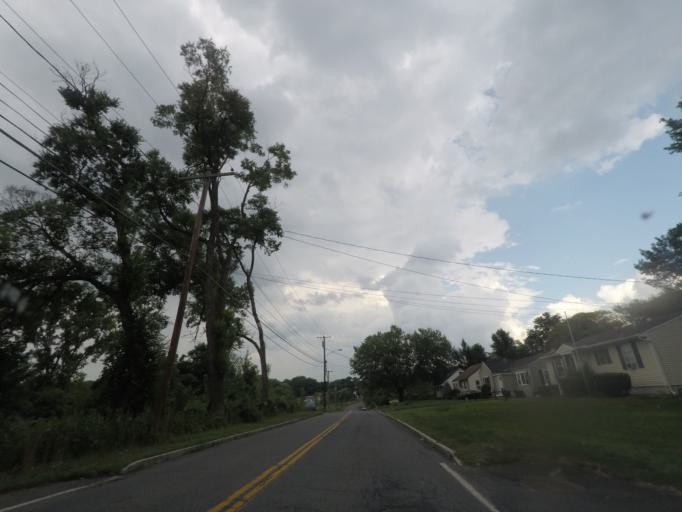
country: US
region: New York
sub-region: Albany County
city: West Albany
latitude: 42.6899
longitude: -73.7800
